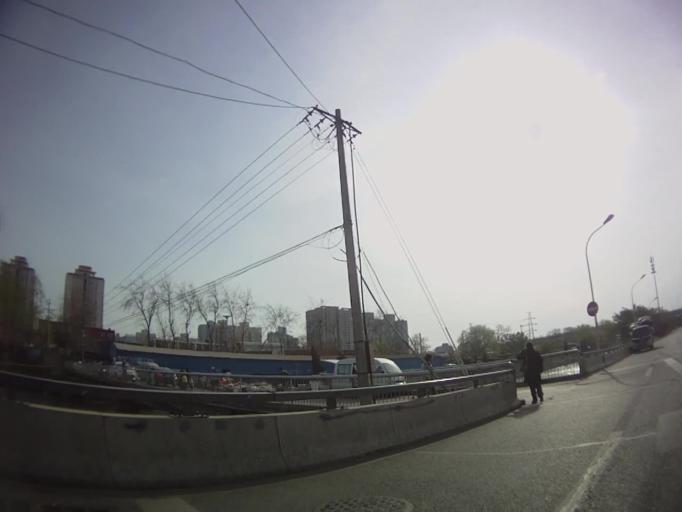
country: CN
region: Beijing
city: Chaowai
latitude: 39.9021
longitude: 116.4424
